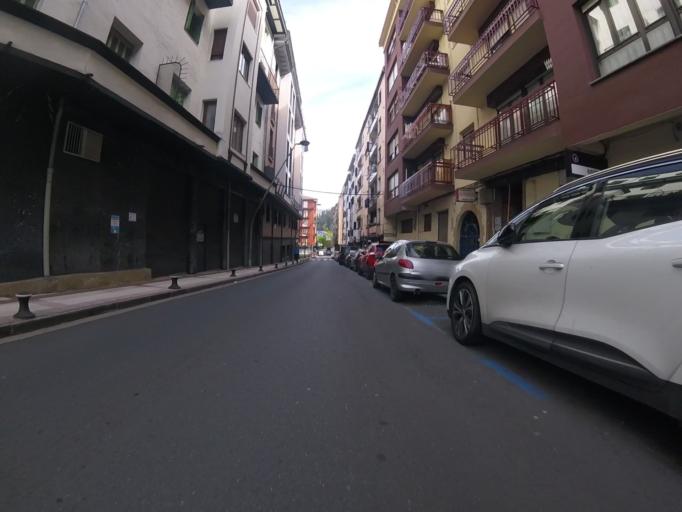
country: ES
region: Basque Country
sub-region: Provincia de Guipuzcoa
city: Zumarraga
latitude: 43.0893
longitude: -2.3129
